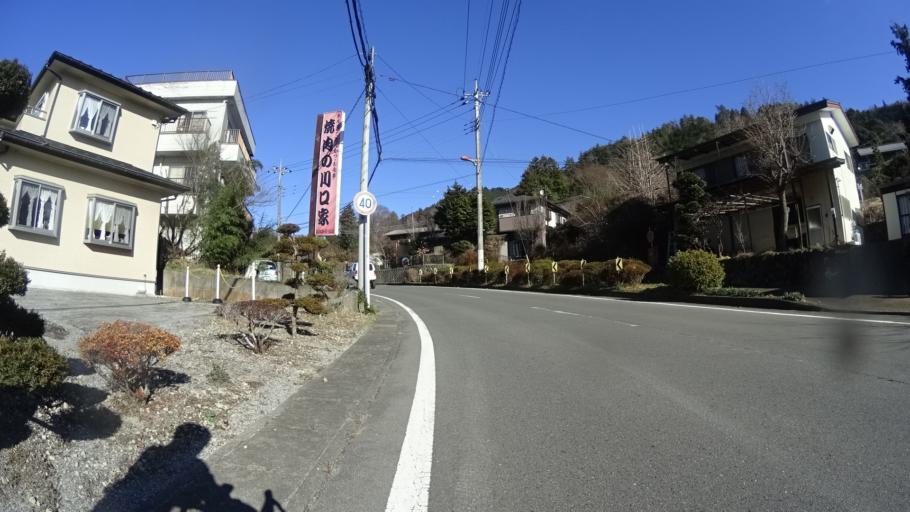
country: JP
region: Yamanashi
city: Uenohara
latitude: 35.6517
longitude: 139.1209
